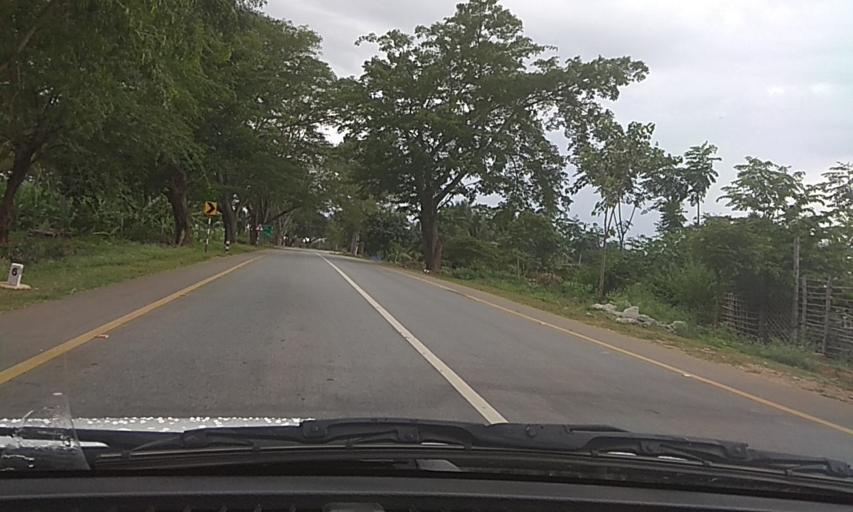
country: IN
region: Karnataka
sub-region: Tumkur
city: Kunigal
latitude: 12.9202
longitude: 77.0320
